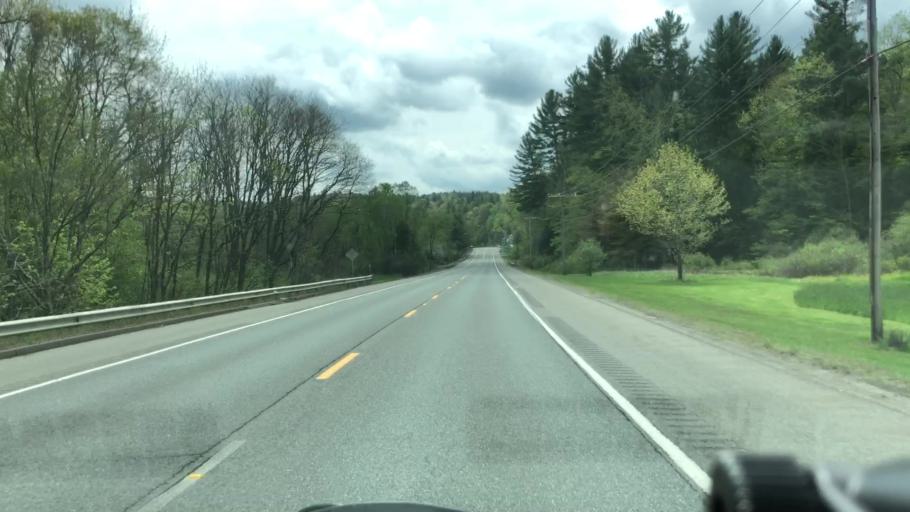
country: US
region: Massachusetts
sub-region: Hampshire County
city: Chesterfield
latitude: 42.4682
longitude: -72.9068
